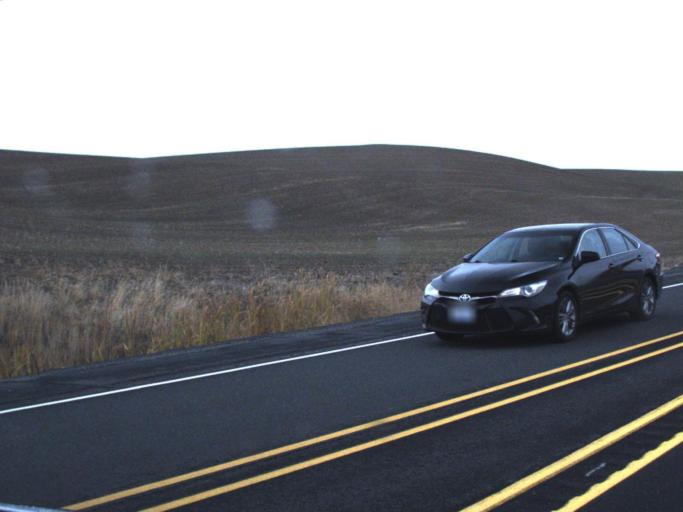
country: US
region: Washington
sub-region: Whitman County
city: Pullman
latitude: 46.7380
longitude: -117.2271
